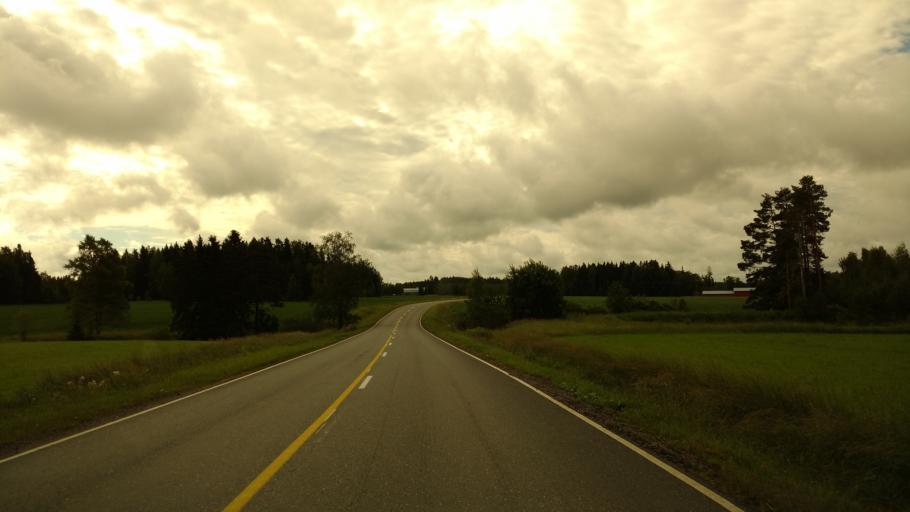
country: FI
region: Varsinais-Suomi
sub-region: Loimaa
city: Koski Tl
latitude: 60.5920
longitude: 23.1309
